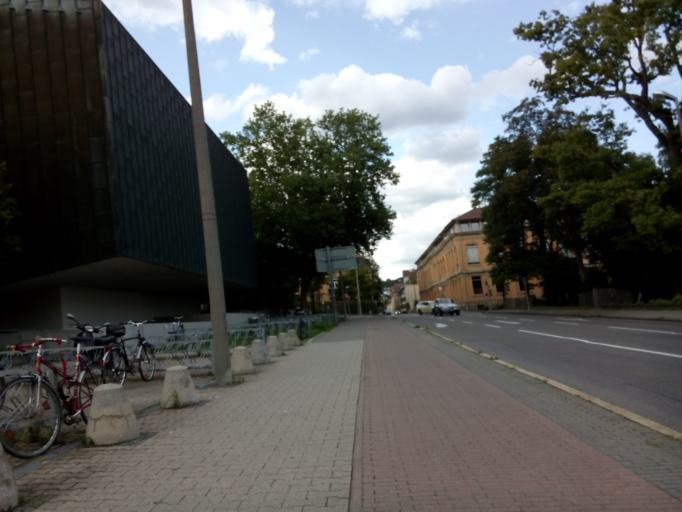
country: DE
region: Baden-Wuerttemberg
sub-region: Tuebingen Region
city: Tuebingen
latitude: 48.5249
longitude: 9.0597
